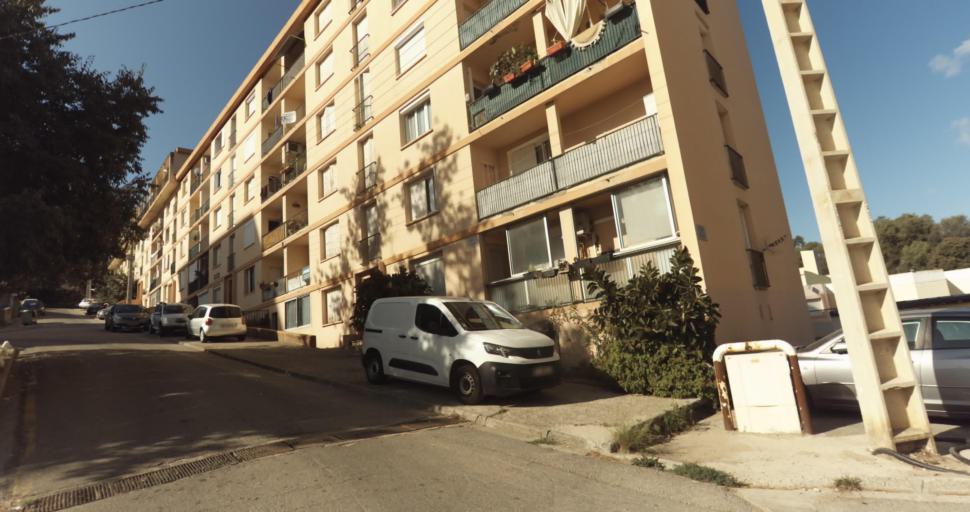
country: FR
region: Corsica
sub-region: Departement de la Corse-du-Sud
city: Ajaccio
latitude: 41.9271
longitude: 8.7280
